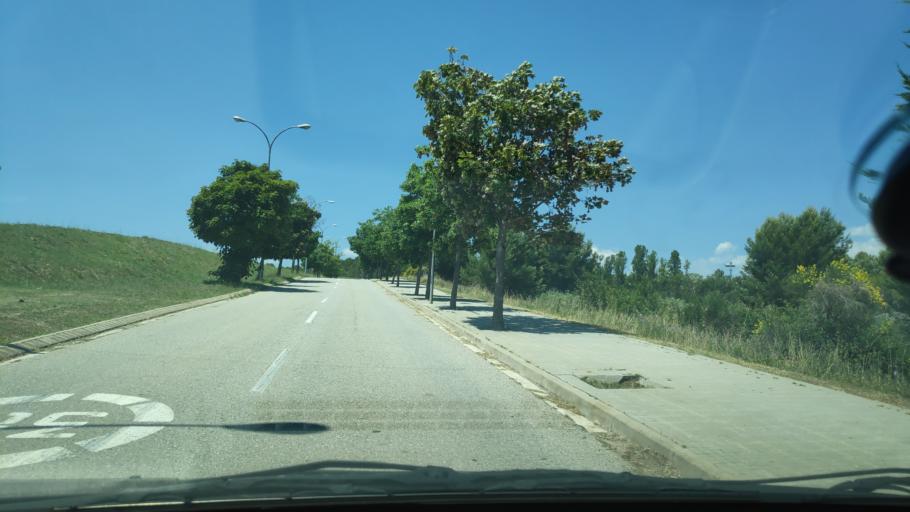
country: ES
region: Catalonia
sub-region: Provincia de Barcelona
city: Barbera del Valles
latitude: 41.4969
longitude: 2.1023
